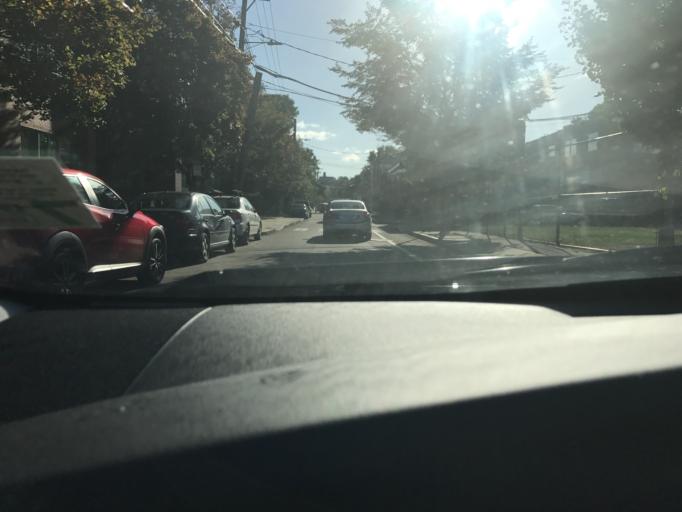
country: US
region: Massachusetts
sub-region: Middlesex County
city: Cambridge
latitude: 42.3582
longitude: -71.1051
